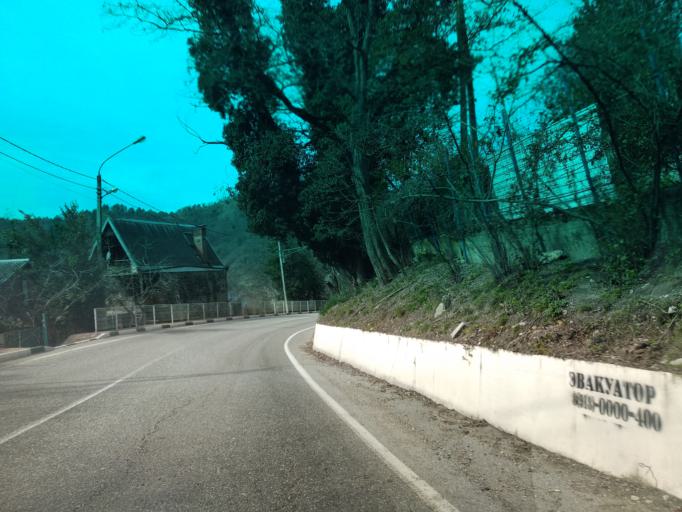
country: RU
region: Krasnodarskiy
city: Shepsi
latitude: 44.0552
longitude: 39.1350
